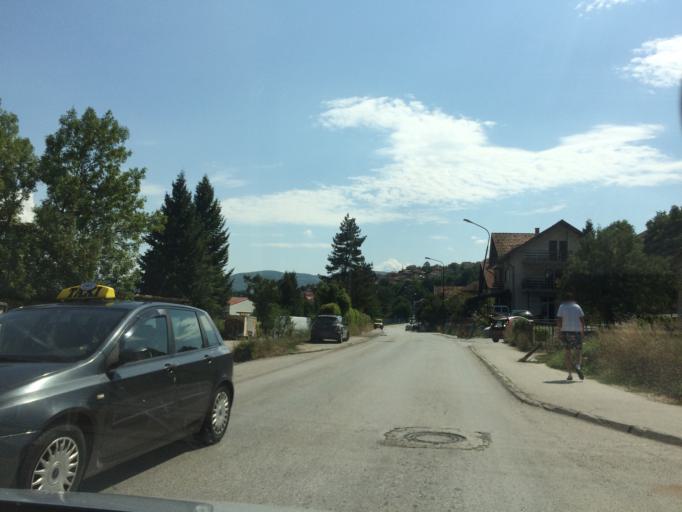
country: RS
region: Central Serbia
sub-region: Zlatiborski Okrug
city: Prijepolje
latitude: 43.3690
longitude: 19.6283
